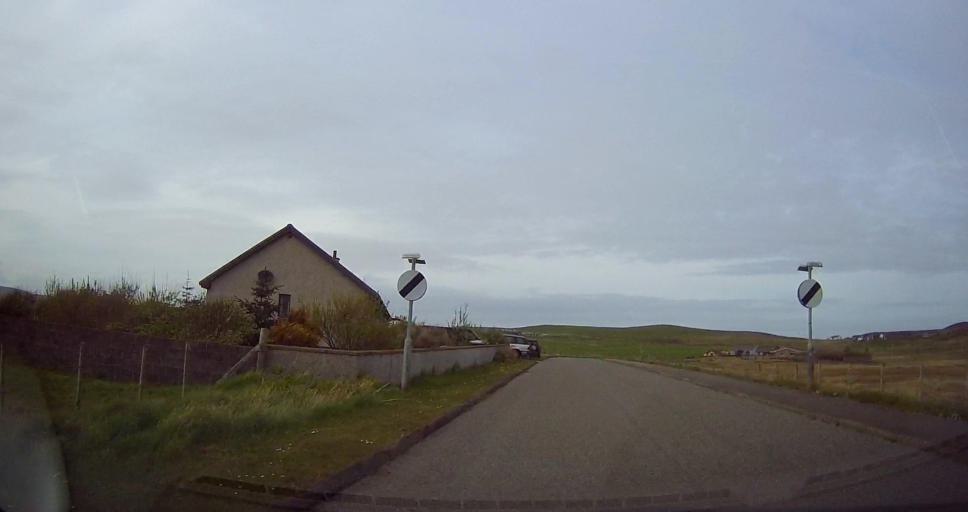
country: GB
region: Scotland
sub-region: Shetland Islands
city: Shetland
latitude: 60.1555
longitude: -1.1159
